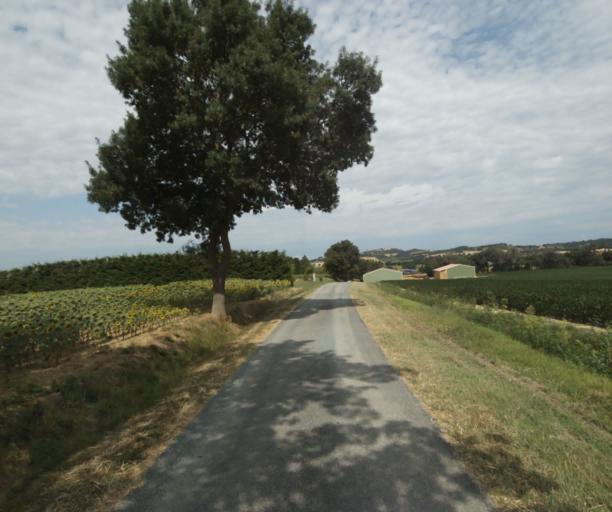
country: FR
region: Midi-Pyrenees
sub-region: Departement de la Haute-Garonne
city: Saint-Felix-Lauragais
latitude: 43.4259
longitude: 1.9117
